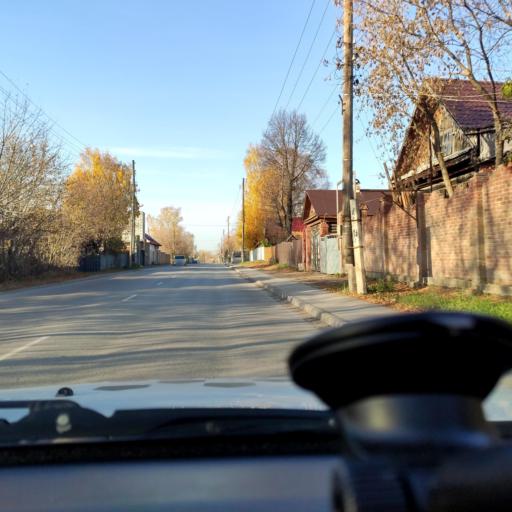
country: RU
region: Perm
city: Perm
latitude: 58.0299
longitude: 56.2288
